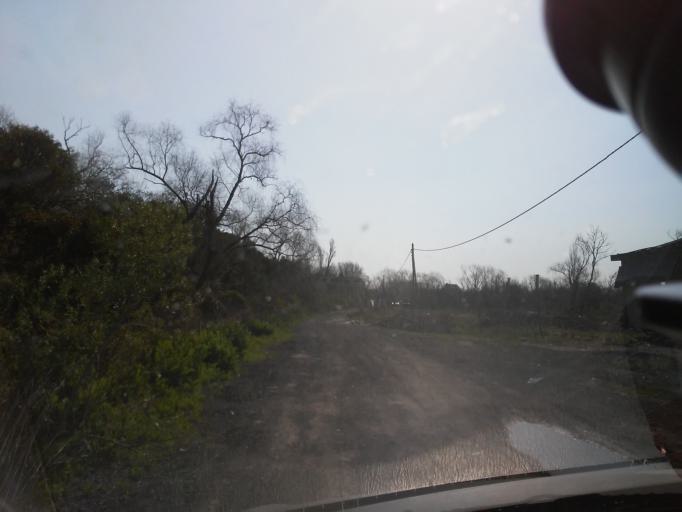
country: AR
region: Buenos Aires
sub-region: Partido de Avellaneda
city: Avellaneda
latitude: -34.6673
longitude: -58.3147
